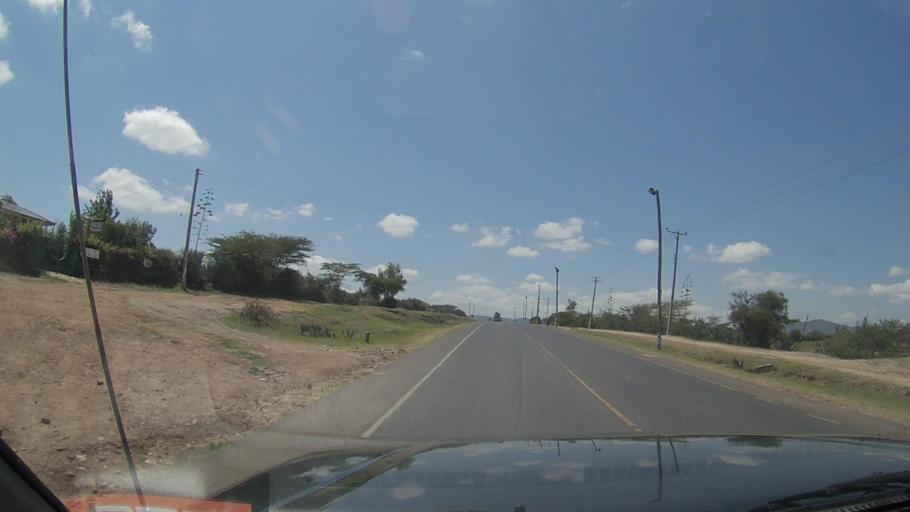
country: KE
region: Machakos
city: Machakos
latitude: -1.5298
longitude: 37.2053
